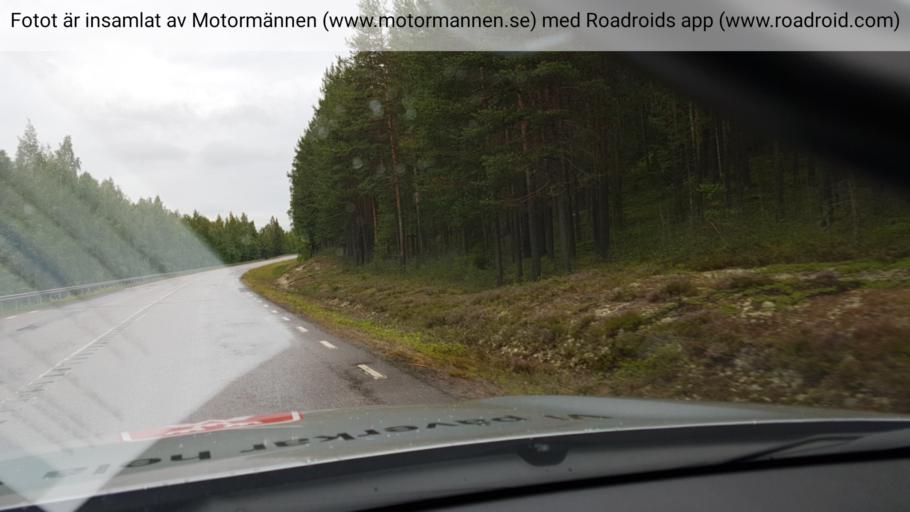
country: SE
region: Norrbotten
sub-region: Alvsbyns Kommun
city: AElvsbyn
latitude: 66.1433
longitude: 20.8789
